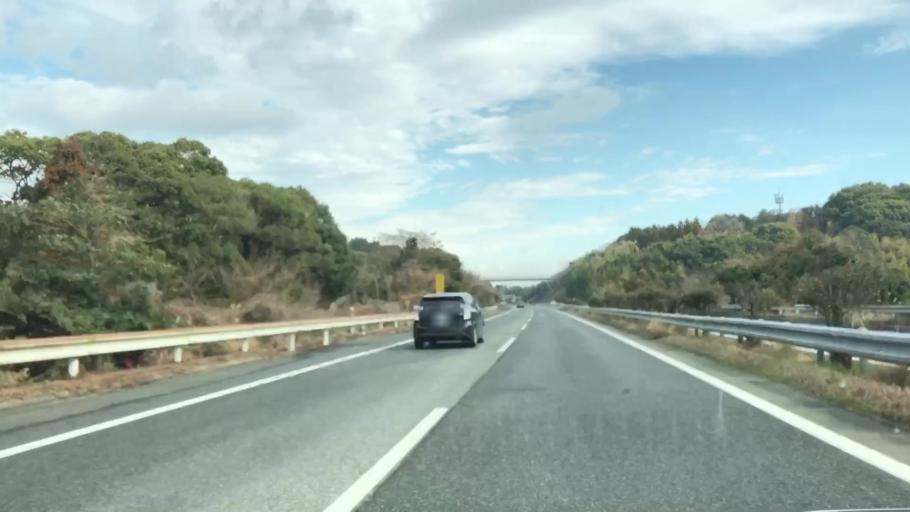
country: JP
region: Saga Prefecture
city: Tosu
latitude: 33.3673
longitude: 130.4565
